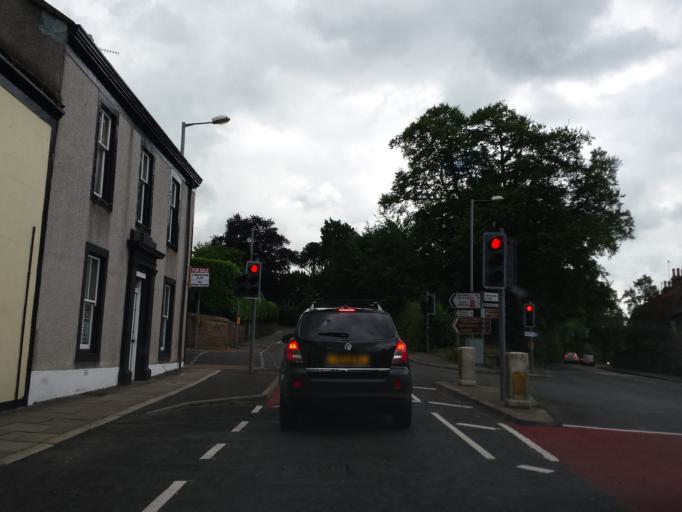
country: GB
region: Scotland
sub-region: Dumfries and Galloway
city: Dumfries
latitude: 55.0611
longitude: -3.6031
